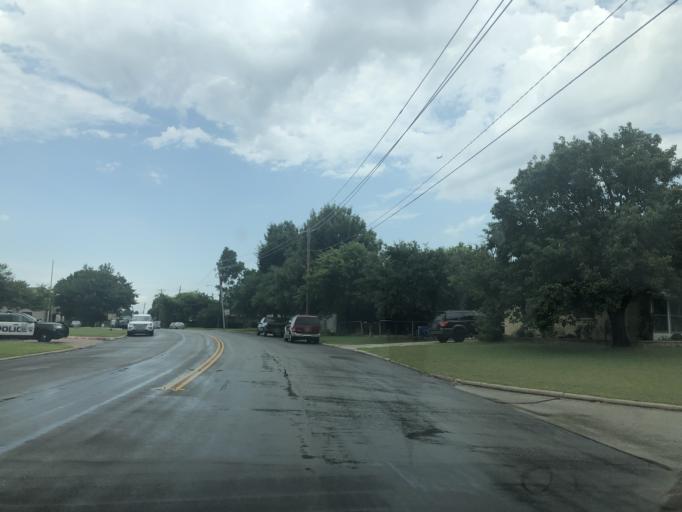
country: US
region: Texas
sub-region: Dallas County
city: Grand Prairie
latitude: 32.7473
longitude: -97.0403
